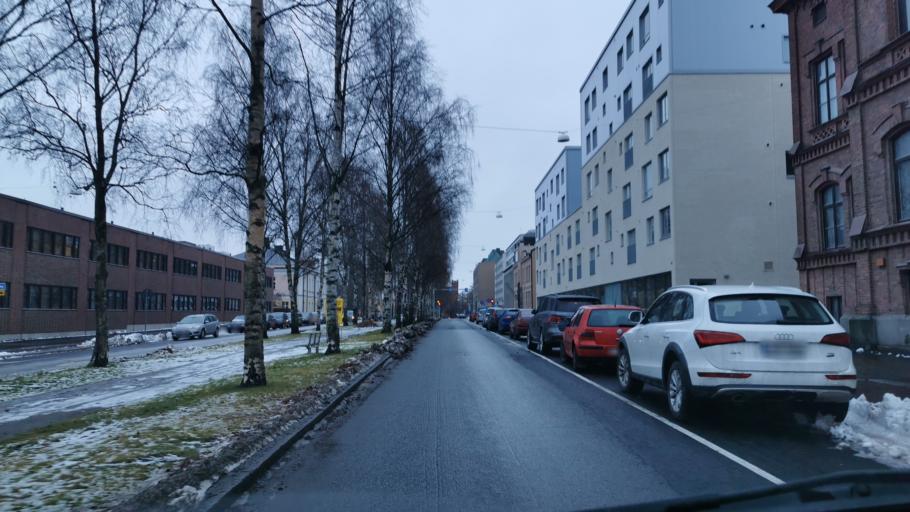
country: FI
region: Ostrobothnia
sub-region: Vaasa
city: Vaasa
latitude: 63.0982
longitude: 21.6069
